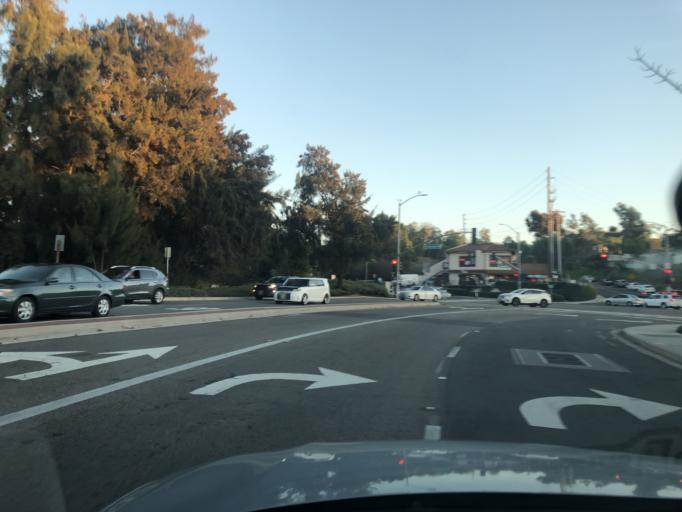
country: US
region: California
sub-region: San Diego County
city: Chula Vista
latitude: 32.6484
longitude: -117.0583
